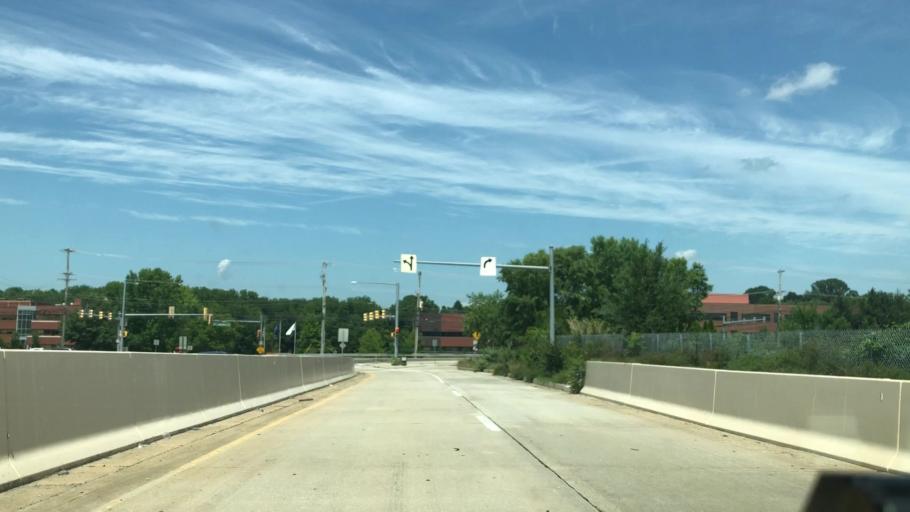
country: US
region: Pennsylvania
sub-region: Montgomery County
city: King of Prussia
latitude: 40.0779
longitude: -75.4159
